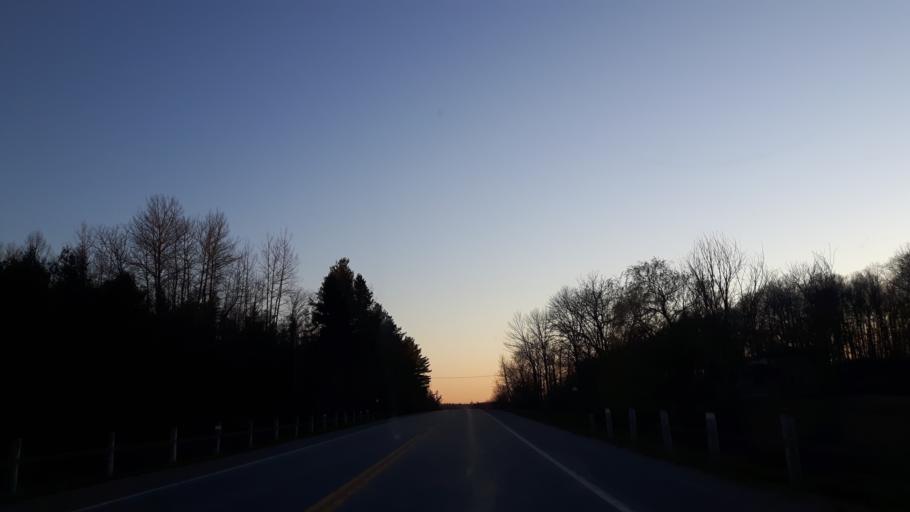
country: CA
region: Ontario
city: Bluewater
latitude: 43.5933
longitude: -81.5693
